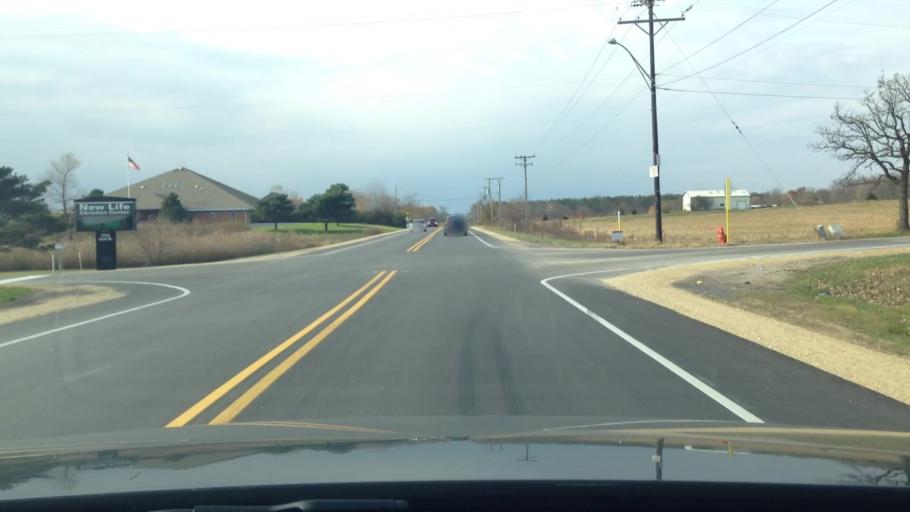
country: US
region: Illinois
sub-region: McHenry County
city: Woodstock
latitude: 42.2551
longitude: -88.4461
